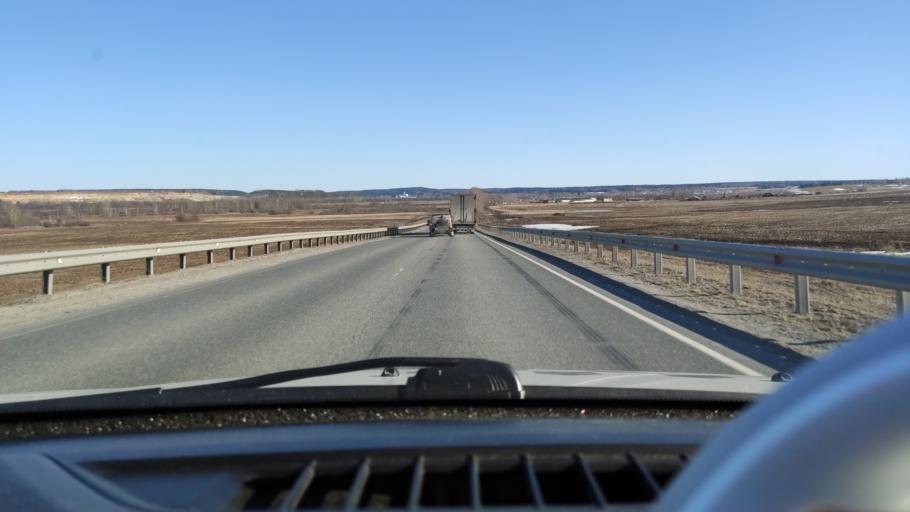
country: RU
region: Perm
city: Kukushtan
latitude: 57.5235
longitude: 56.6263
